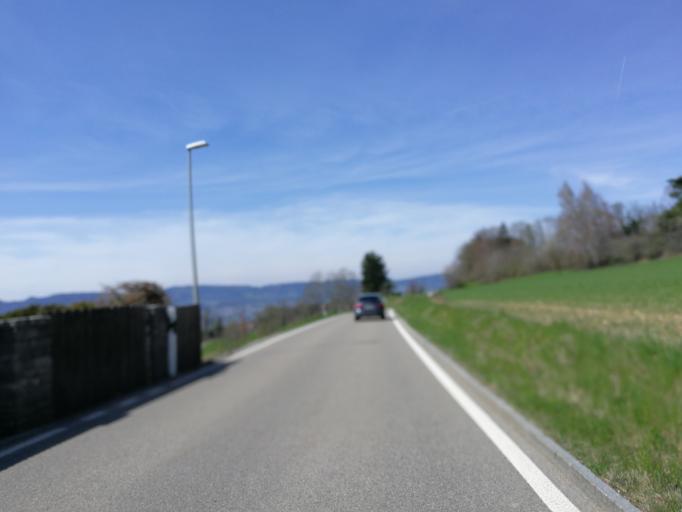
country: CH
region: Zurich
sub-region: Bezirk Meilen
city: Obermeilen
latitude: 47.2857
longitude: 8.6631
